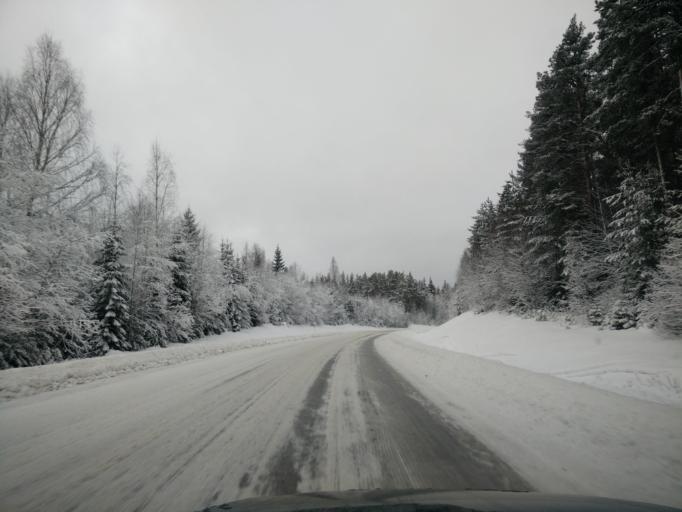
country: SE
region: Vaesternorrland
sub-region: Ange Kommun
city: Ange
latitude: 62.4025
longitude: 15.4802
